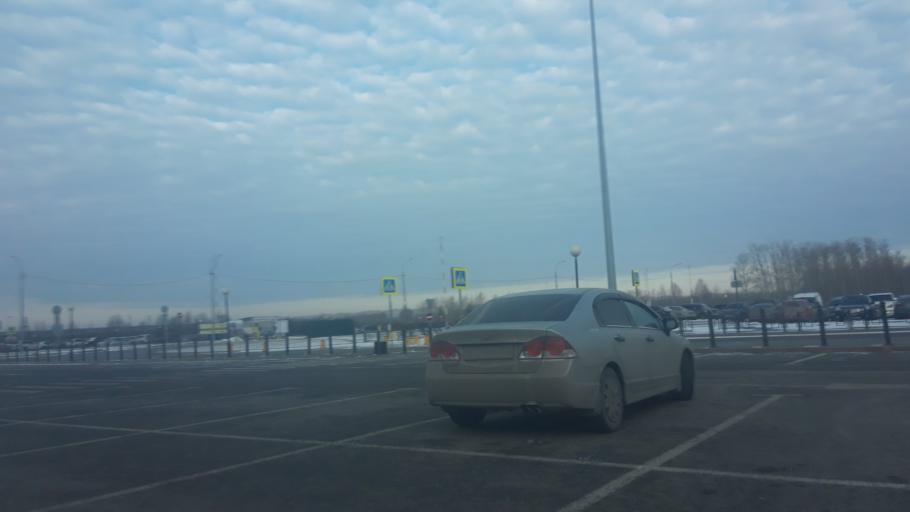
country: RU
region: Tjumen
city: Moskovskiy
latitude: 57.1820
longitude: 65.3493
